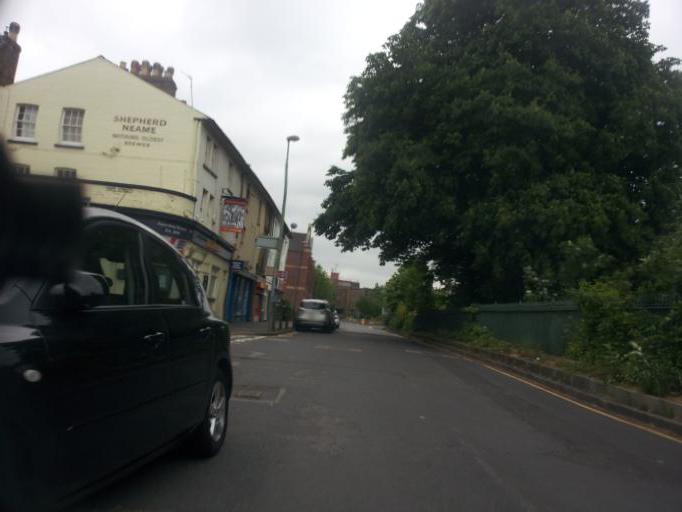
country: GB
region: England
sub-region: Kent
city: Maidstone
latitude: 51.2806
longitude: 0.5196
